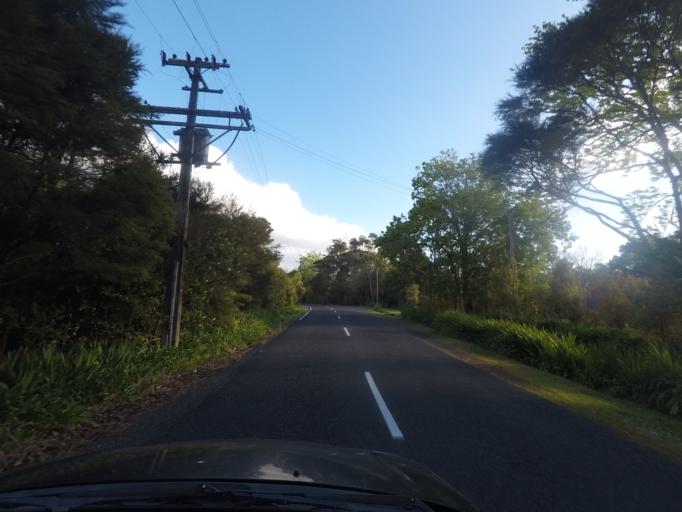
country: NZ
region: Auckland
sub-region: Auckland
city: Waitakere
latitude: -36.9201
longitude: 174.6154
